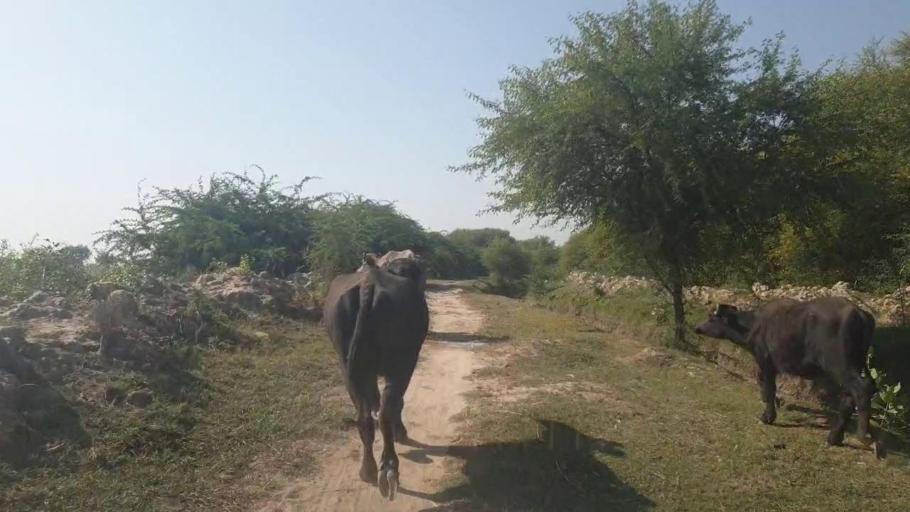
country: PK
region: Sindh
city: Badin
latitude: 24.7248
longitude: 68.8786
